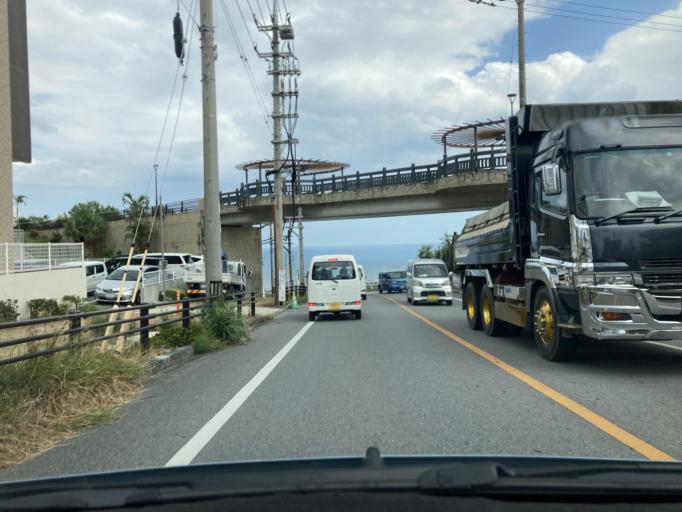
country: JP
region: Okinawa
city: Ginowan
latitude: 26.2498
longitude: 127.7748
